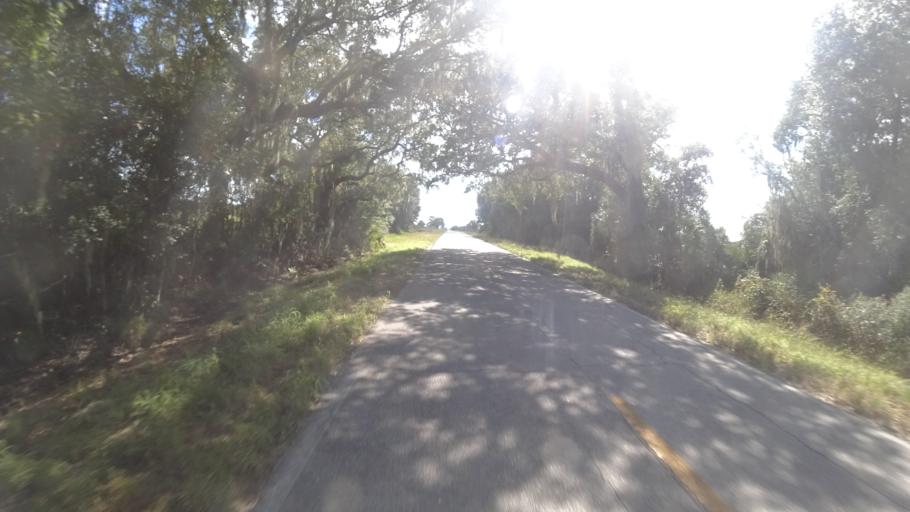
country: US
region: Florida
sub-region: Sarasota County
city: North Port
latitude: 27.2088
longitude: -82.1222
